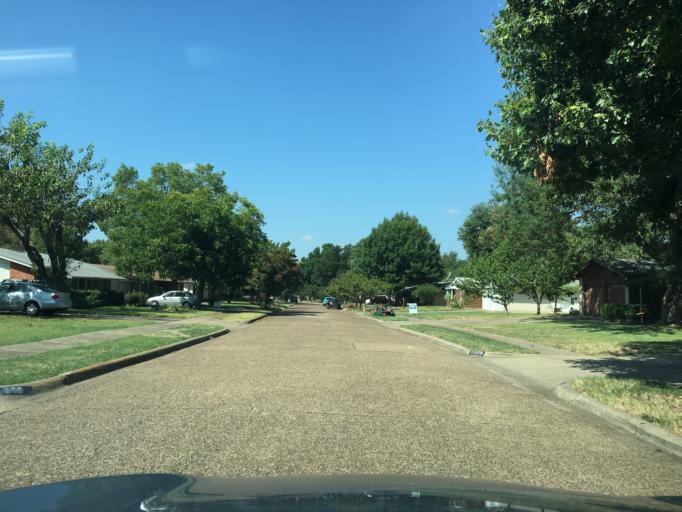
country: US
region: Texas
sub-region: Dallas County
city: Garland
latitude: 32.8616
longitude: -96.6844
